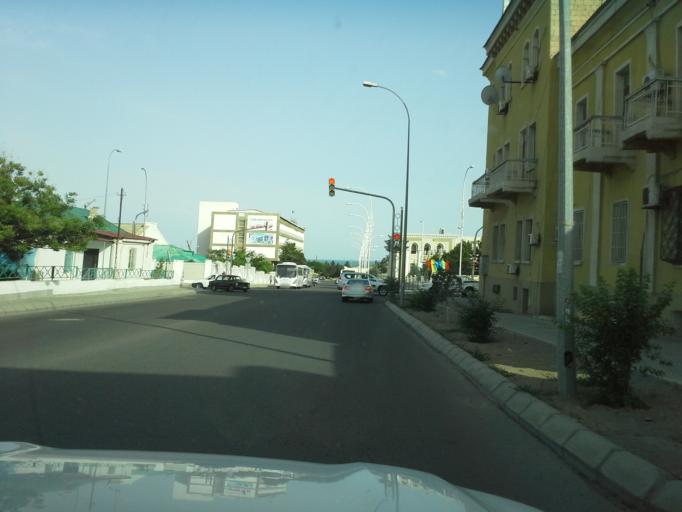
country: TM
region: Balkan
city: Turkmenbasy
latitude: 40.0066
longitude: 52.9932
